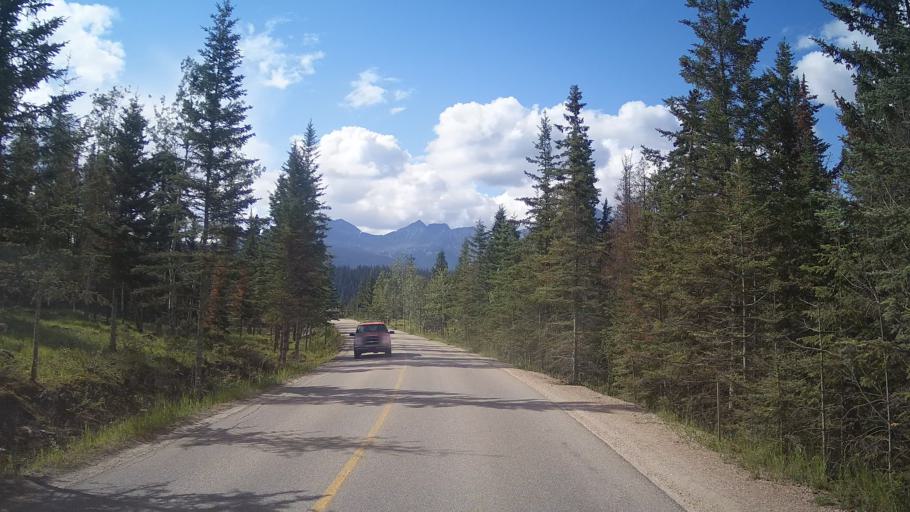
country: CA
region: Alberta
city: Jasper Park Lodge
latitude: 52.8670
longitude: -118.0714
